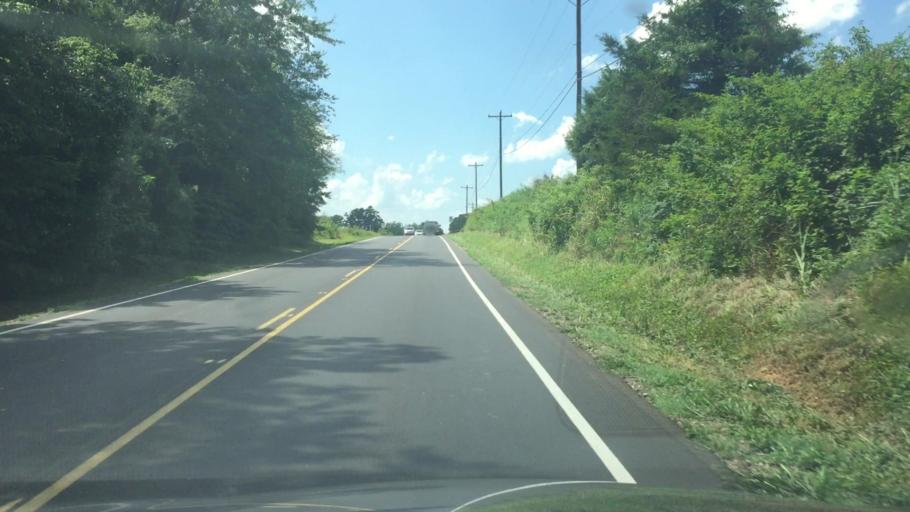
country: US
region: North Carolina
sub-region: Iredell County
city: Mooresville
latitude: 35.5914
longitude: -80.7548
